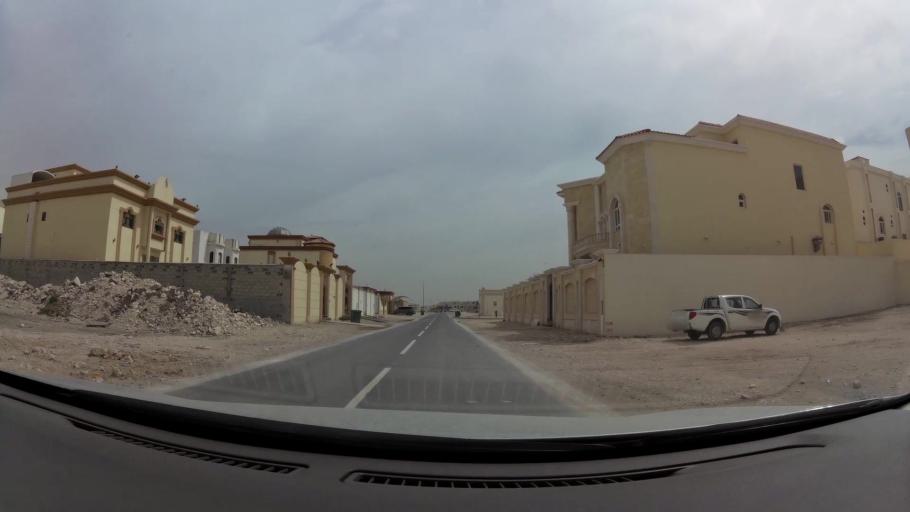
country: QA
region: Baladiyat ad Dawhah
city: Doha
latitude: 25.2163
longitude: 51.4668
